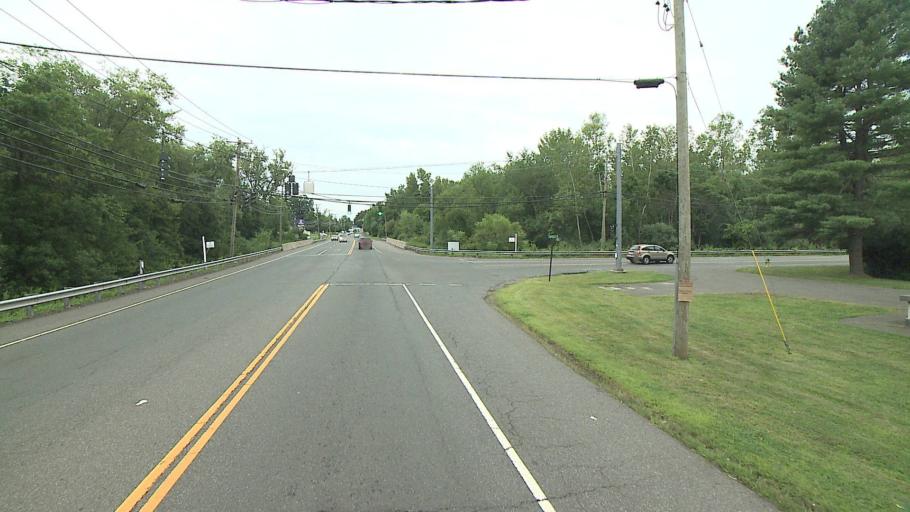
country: US
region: Connecticut
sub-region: Middlesex County
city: Cromwell
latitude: 41.5949
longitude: -72.6767
